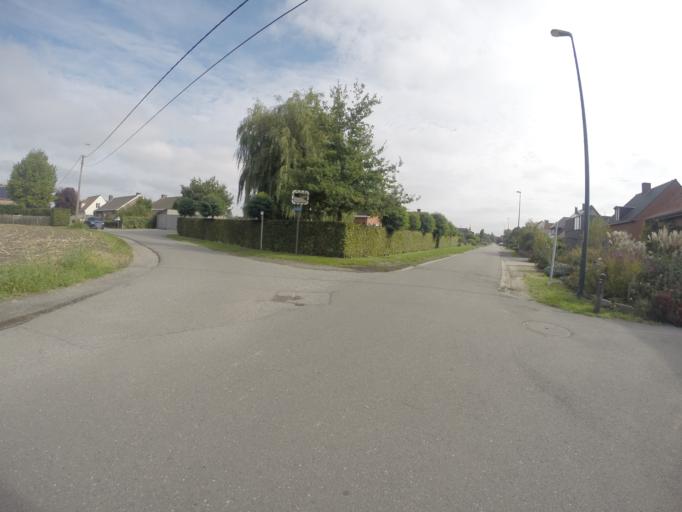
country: BE
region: Flanders
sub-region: Provincie Oost-Vlaanderen
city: Aalter
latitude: 51.0723
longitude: 3.4357
